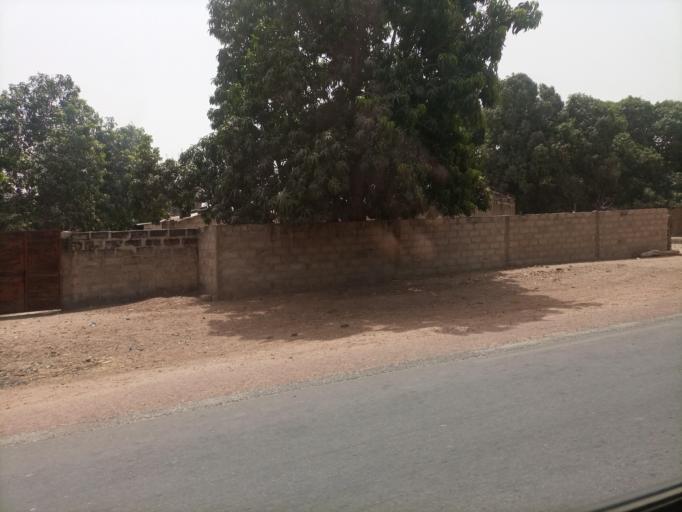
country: SN
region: Fatick
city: Sokone
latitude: 13.7273
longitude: -16.4230
